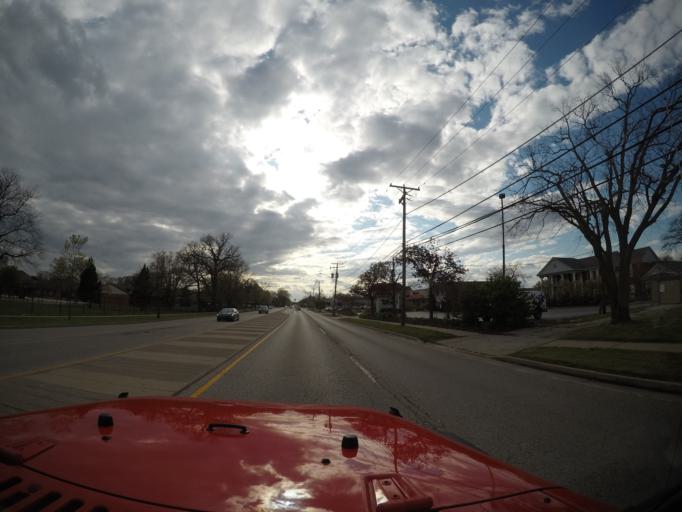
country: US
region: Illinois
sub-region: Cook County
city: Glenview
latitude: 42.0800
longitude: -87.7959
